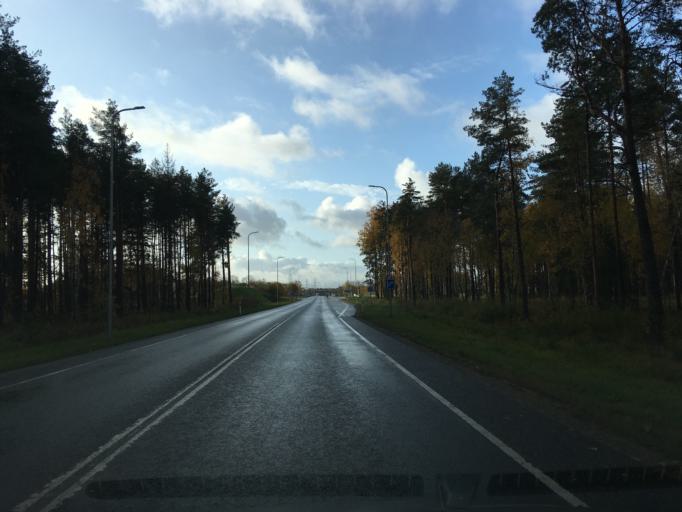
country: EE
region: Harju
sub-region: Saue vald
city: Laagri
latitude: 59.3559
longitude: 24.6003
